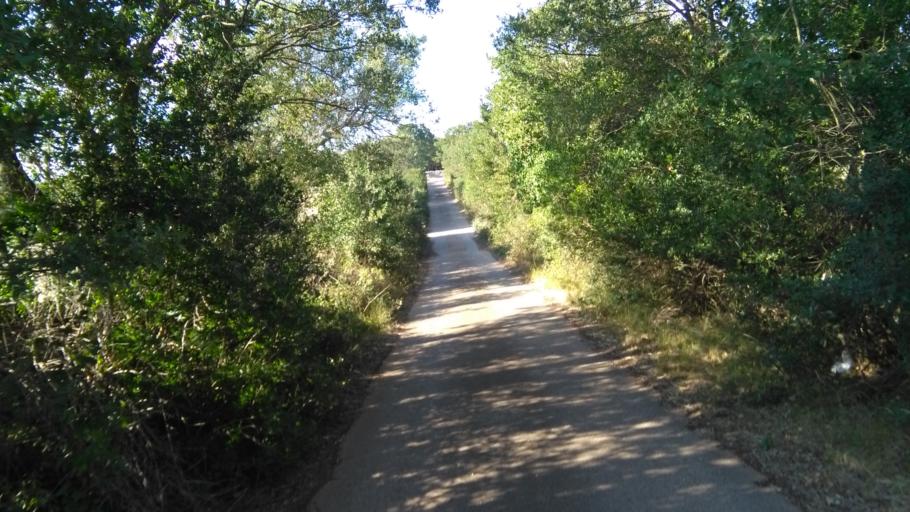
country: IT
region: Apulia
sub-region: Provincia di Bari
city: Putignano
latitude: 40.8192
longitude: 17.0595
